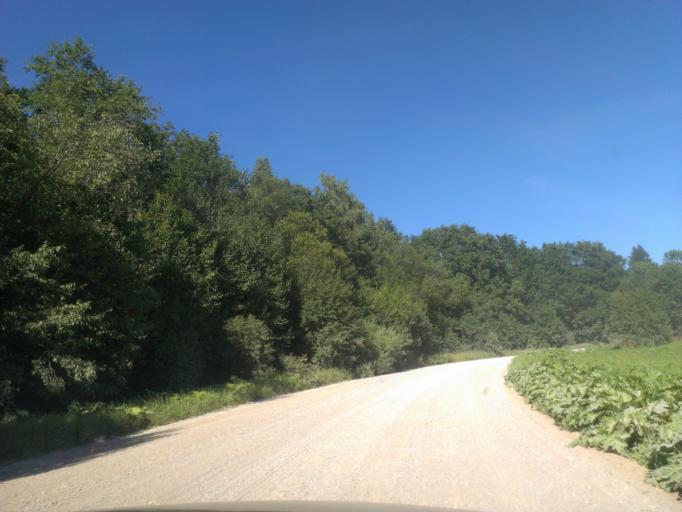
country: LV
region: Malpils
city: Malpils
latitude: 57.0595
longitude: 25.1428
